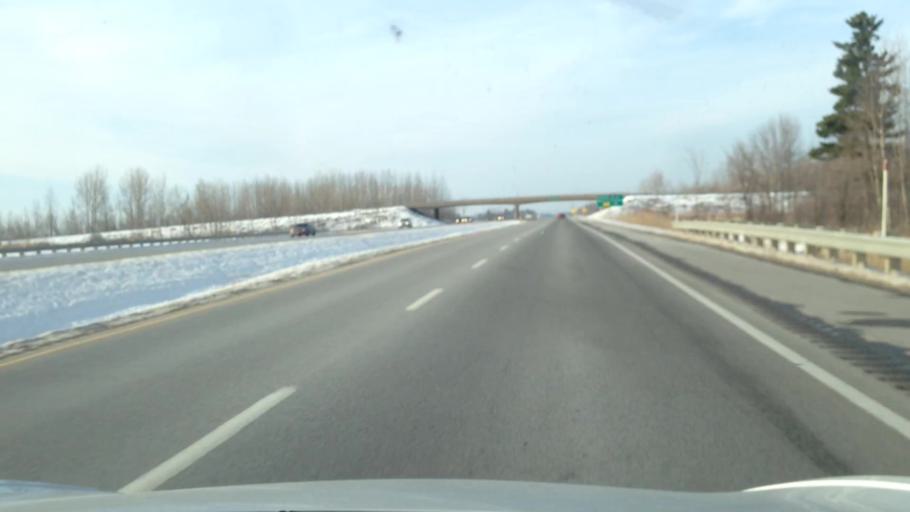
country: CA
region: Quebec
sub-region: Monteregie
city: Rigaud
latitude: 45.4906
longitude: -74.3471
